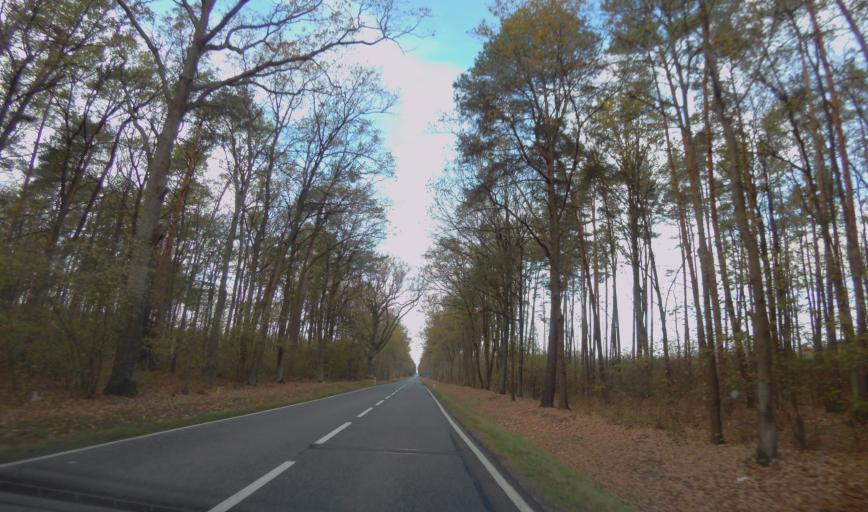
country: PL
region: Subcarpathian Voivodeship
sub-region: Powiat nizanski
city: Krzeszow
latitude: 50.3866
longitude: 22.3069
